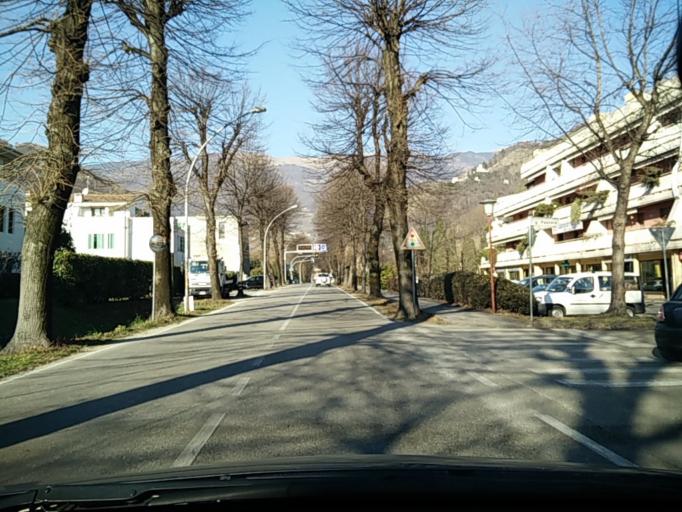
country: IT
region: Veneto
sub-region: Provincia di Treviso
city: Vittorio Veneto
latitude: 45.9935
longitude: 12.2963
